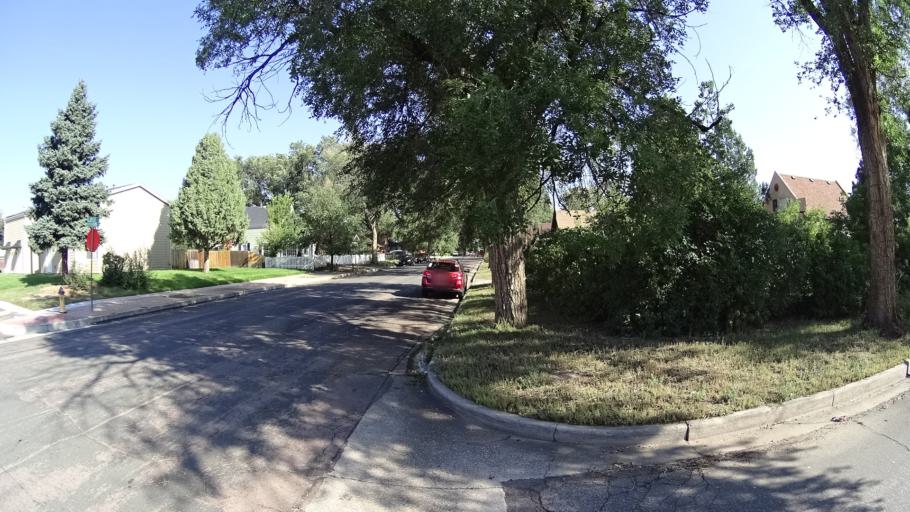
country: US
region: Colorado
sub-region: El Paso County
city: Colorado Springs
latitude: 38.8700
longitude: -104.8255
